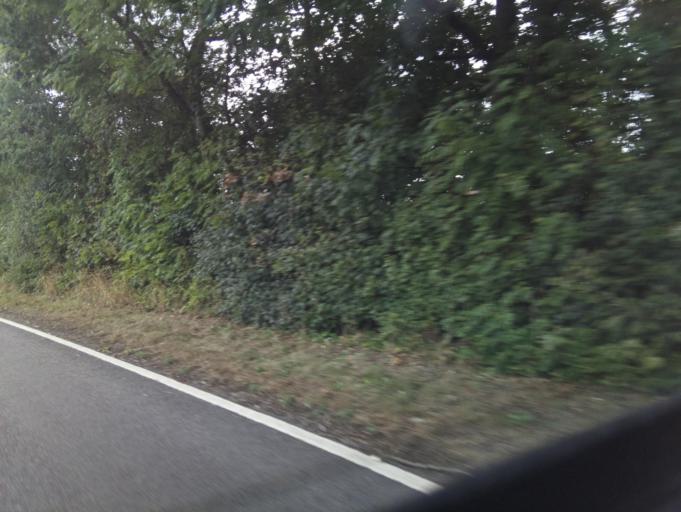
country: GB
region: England
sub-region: Leicestershire
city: Coalville
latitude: 52.7588
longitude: -1.3776
